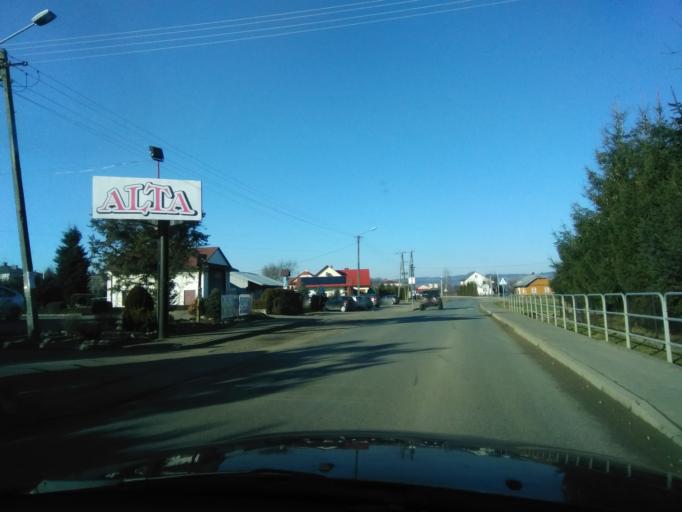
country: PL
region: Subcarpathian Voivodeship
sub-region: Powiat brzozowski
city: Haczow
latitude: 49.6727
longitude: 21.8877
